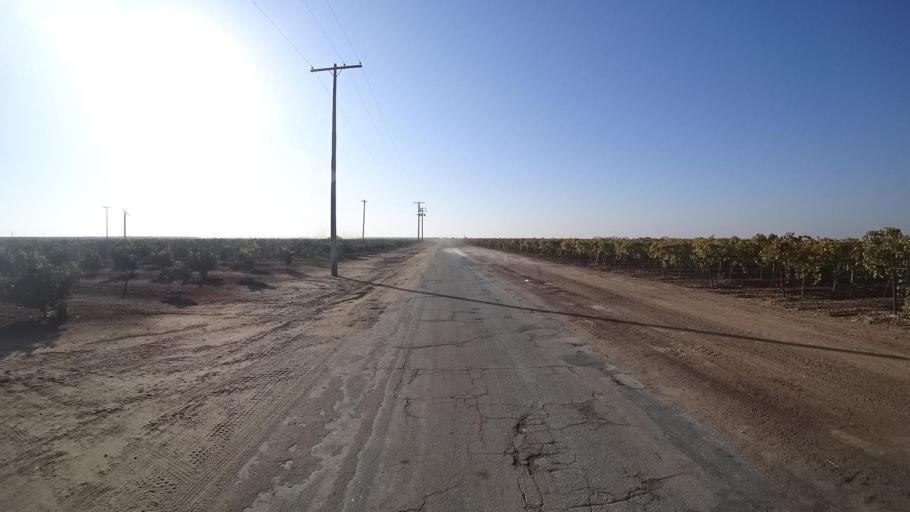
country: US
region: California
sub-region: Tulare County
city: Richgrove
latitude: 35.7705
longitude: -119.1607
